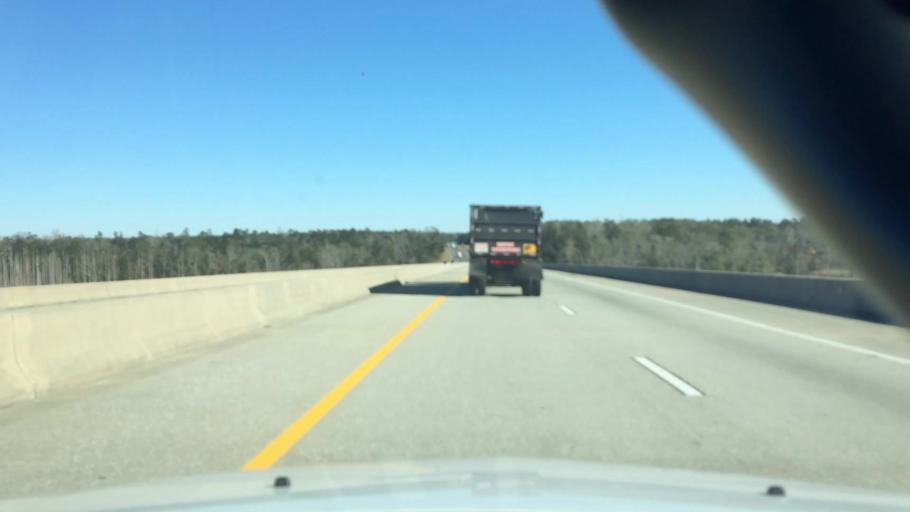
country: US
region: North Carolina
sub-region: New Hanover County
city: Wrightsboro
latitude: 34.3024
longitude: -77.9563
